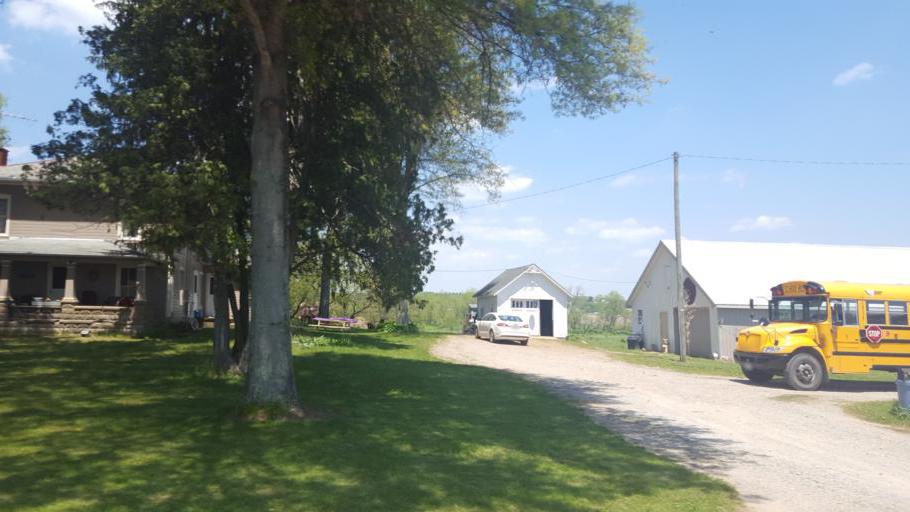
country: US
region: Ohio
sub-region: Knox County
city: Oak Hill
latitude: 40.2908
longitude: -82.2904
